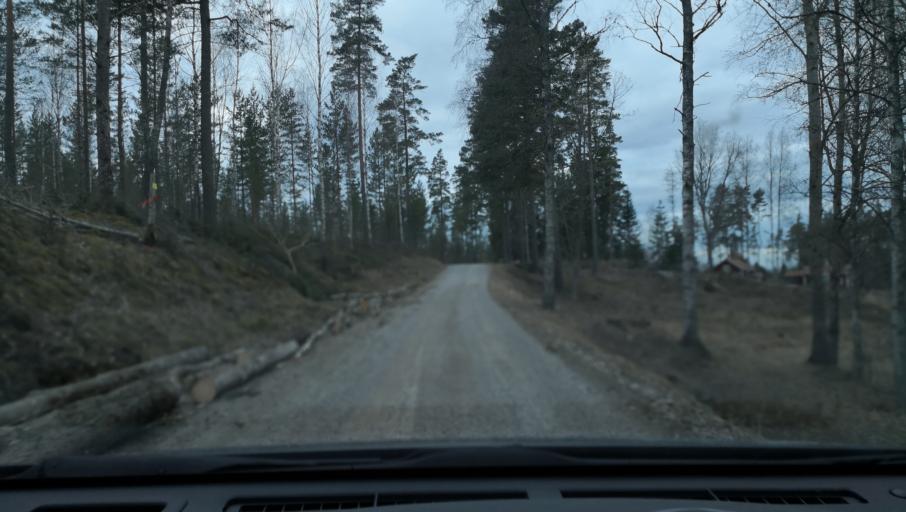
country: SE
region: Soedermanland
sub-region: Katrineholms Kommun
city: Katrineholm
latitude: 59.1322
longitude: 16.1500
